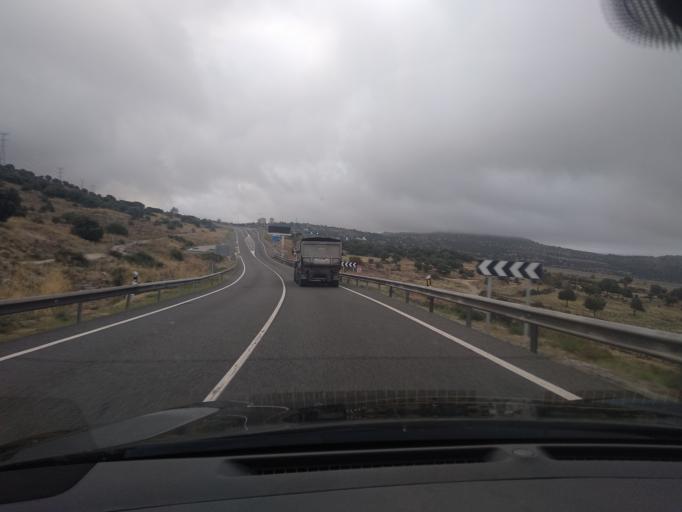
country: ES
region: Castille and Leon
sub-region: Provincia de Segovia
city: Otero de Herreros
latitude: 40.7944
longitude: -4.2164
